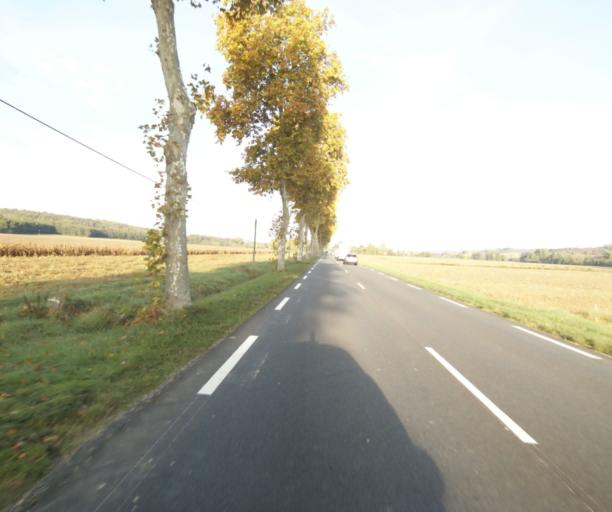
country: FR
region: Midi-Pyrenees
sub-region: Departement du Tarn-et-Garonne
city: Saint-Nauphary
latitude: 43.9418
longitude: 1.4692
